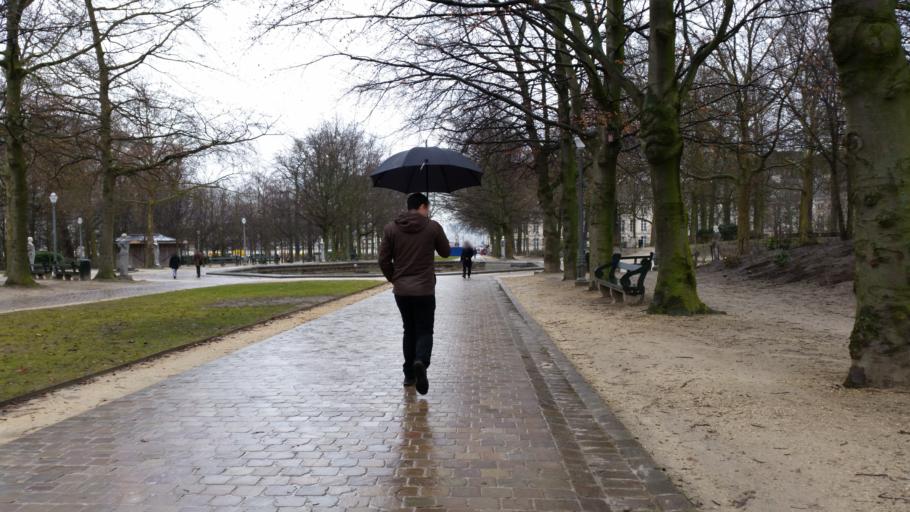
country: BE
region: Brussels Capital
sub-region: Bruxelles-Capitale
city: Brussels
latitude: 50.8436
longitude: 4.3641
